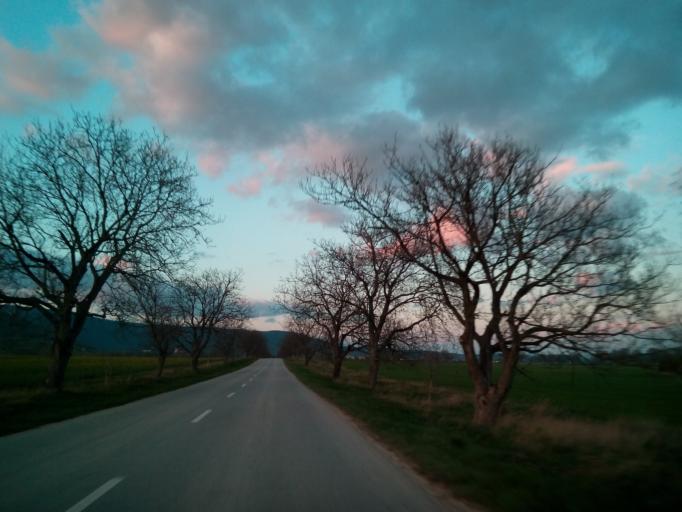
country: SK
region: Kosicky
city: Medzev
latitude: 48.5886
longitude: 20.8554
